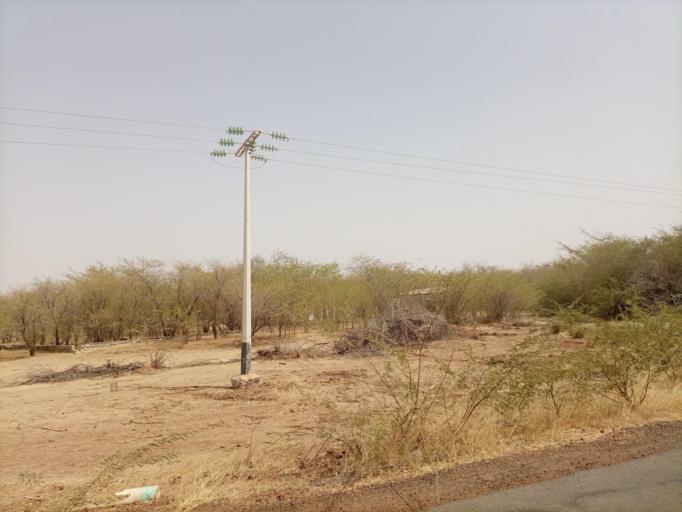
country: SN
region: Fatick
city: Foundiougne
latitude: 14.1883
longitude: -16.4535
